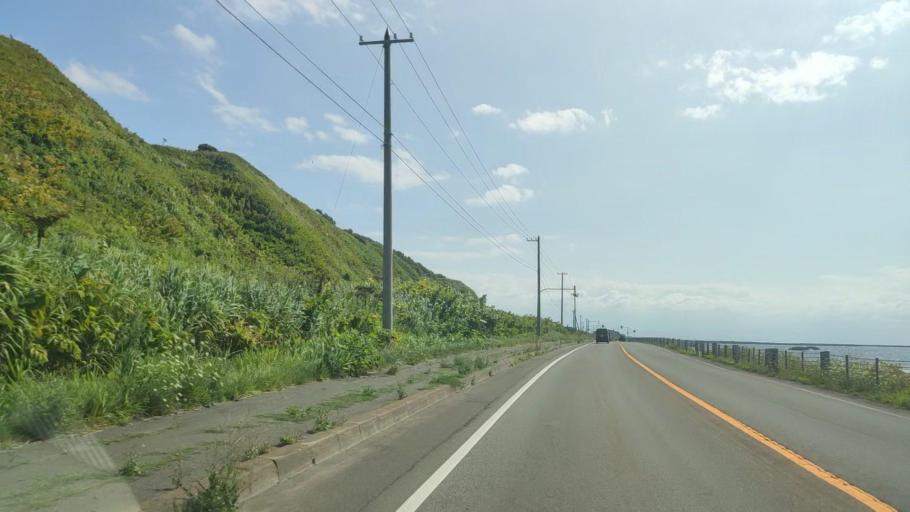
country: JP
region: Hokkaido
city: Rumoi
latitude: 43.9884
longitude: 141.6503
